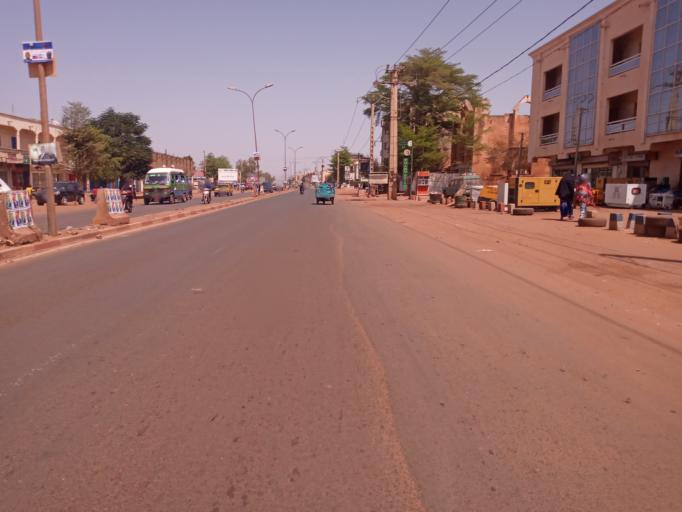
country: ML
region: Bamako
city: Bamako
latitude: 12.6634
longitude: -7.9461
